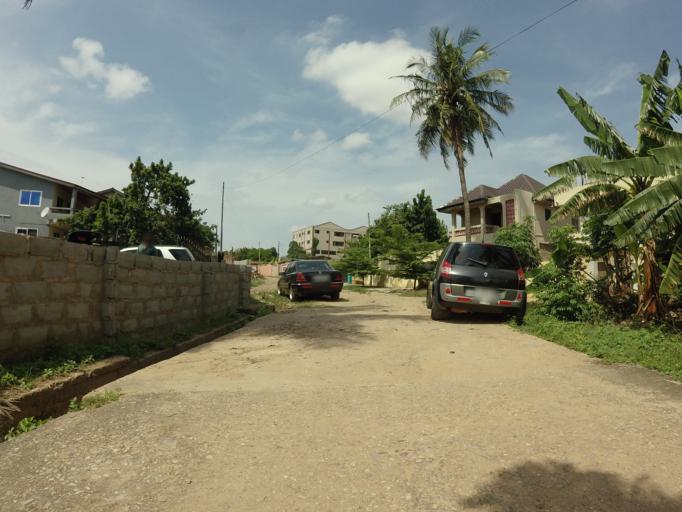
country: GH
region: Greater Accra
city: Dome
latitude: 5.6302
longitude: -0.2343
